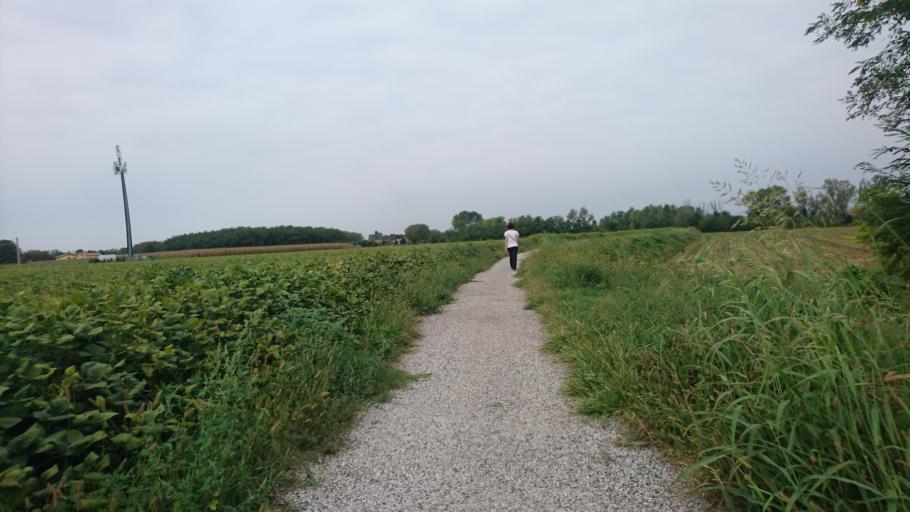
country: IT
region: Veneto
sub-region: Provincia di Padova
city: Piazzola sul Brenta
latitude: 45.5433
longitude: 11.8008
